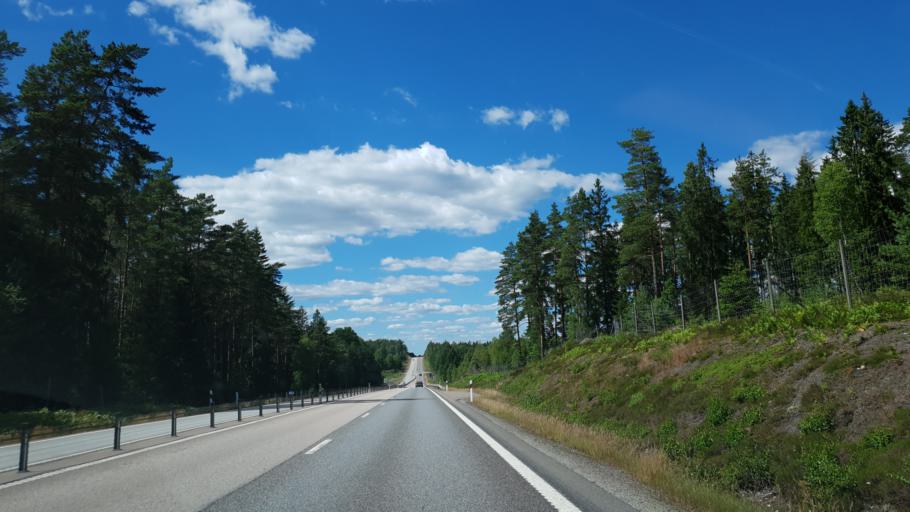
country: SE
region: Kronoberg
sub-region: Lessebo Kommun
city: Hovmantorp
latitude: 56.8455
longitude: 15.0563
